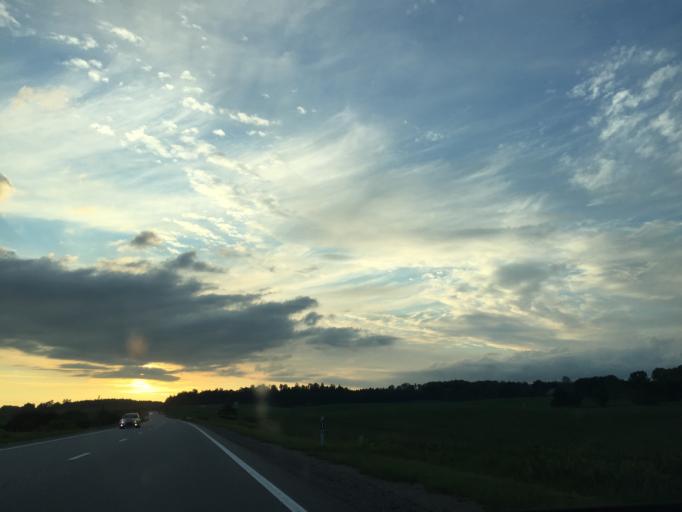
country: LV
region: Tukuma Rajons
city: Tukums
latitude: 56.9772
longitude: 23.0508
